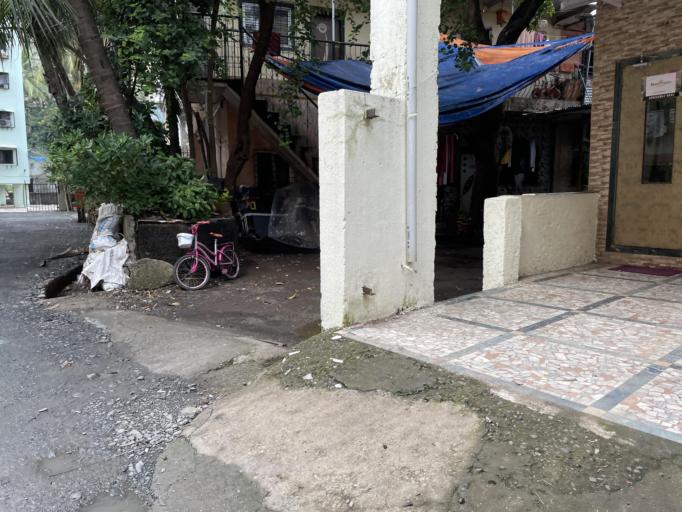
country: IN
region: Maharashtra
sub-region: Mumbai Suburban
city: Borivli
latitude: 19.2564
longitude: 72.8548
